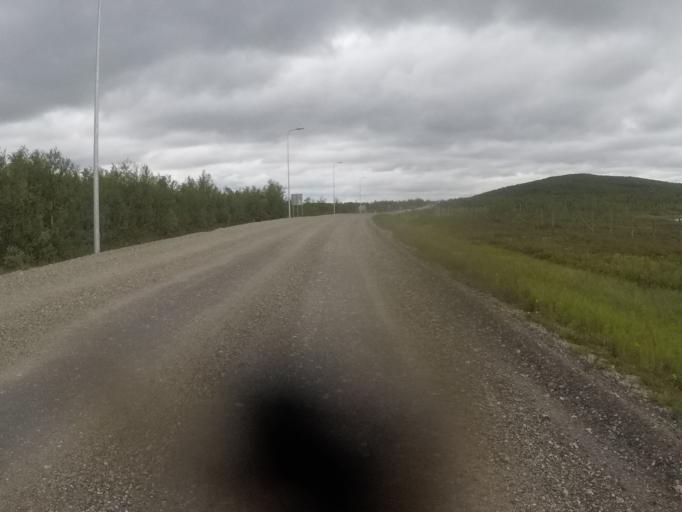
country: FI
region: Lapland
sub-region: Tunturi-Lappi
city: Enontekioe
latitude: 68.6632
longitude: 23.3209
